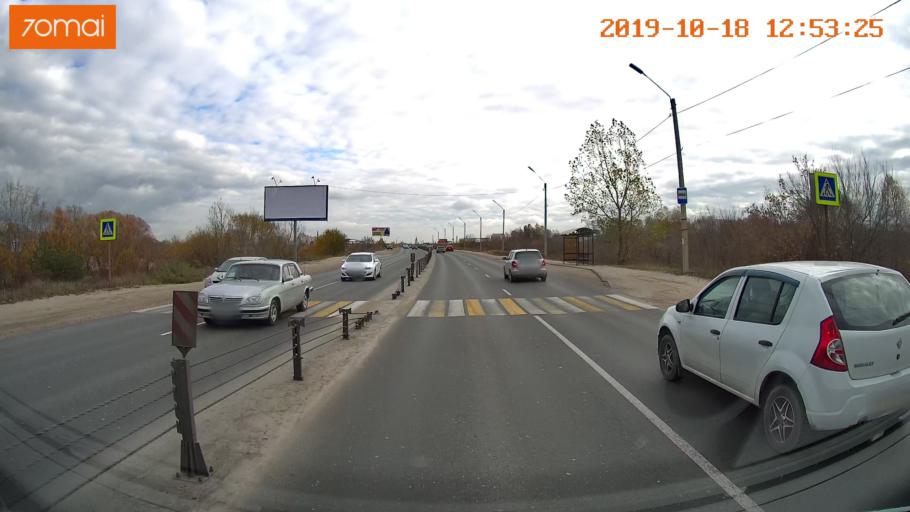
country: RU
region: Rjazan
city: Ryazan'
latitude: 54.6445
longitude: 39.7064
